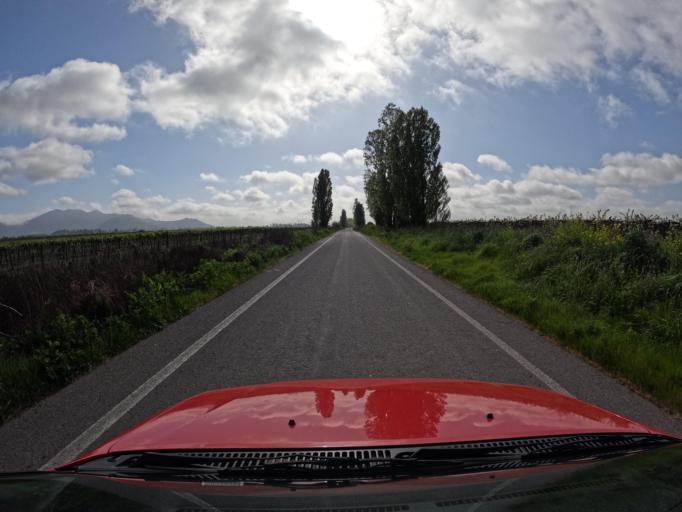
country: CL
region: Maule
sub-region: Provincia de Curico
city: Rauco
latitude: -34.8836
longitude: -71.2494
